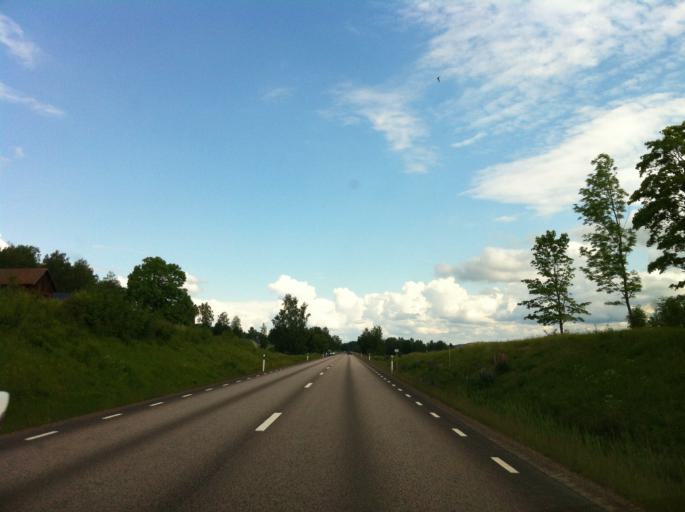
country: SE
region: Vaermland
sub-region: Sunne Kommun
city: Sunne
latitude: 59.9053
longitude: 13.1345
